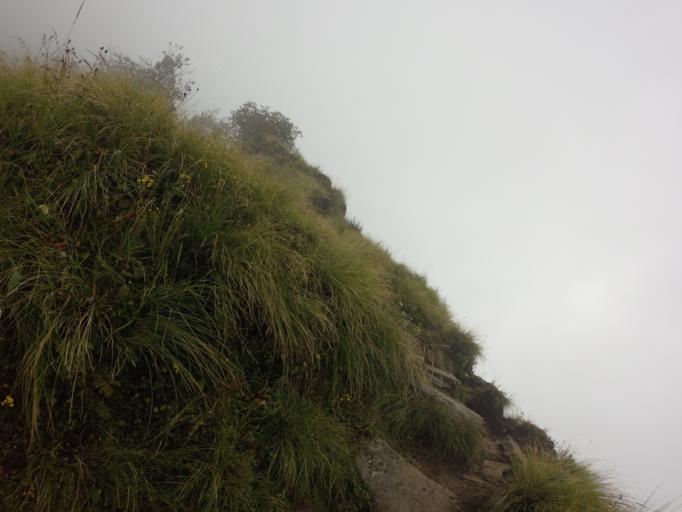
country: NP
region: Western Region
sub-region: Dhawalagiri Zone
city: Chitre
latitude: 28.4177
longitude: 83.8562
